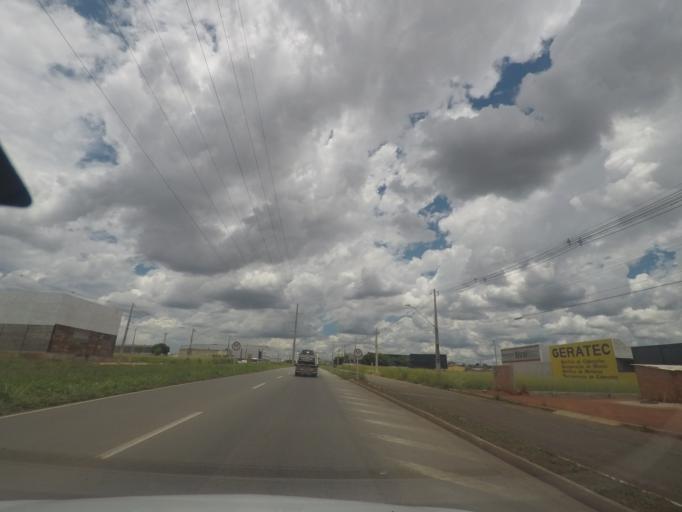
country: BR
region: Goias
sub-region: Goiania
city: Goiania
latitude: -16.7254
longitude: -49.3523
